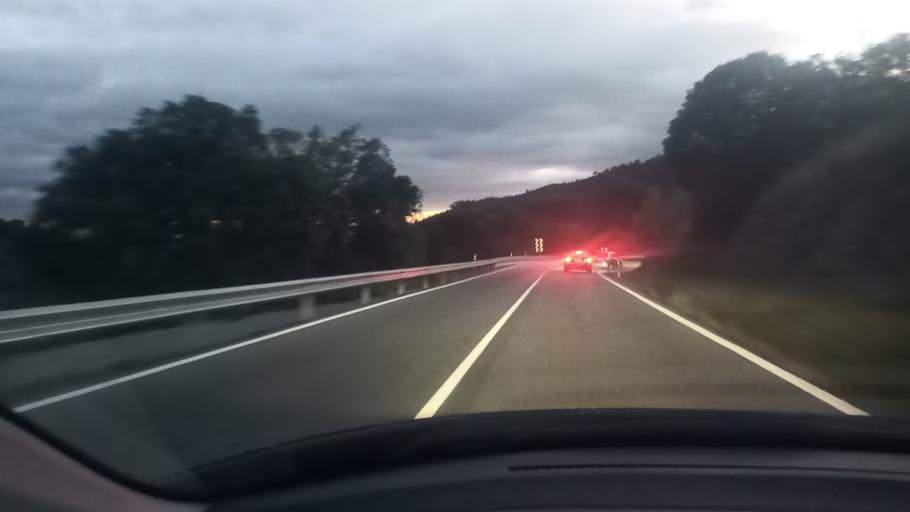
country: ES
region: Madrid
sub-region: Provincia de Madrid
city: Navas del Rey
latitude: 40.4447
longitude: -4.2651
